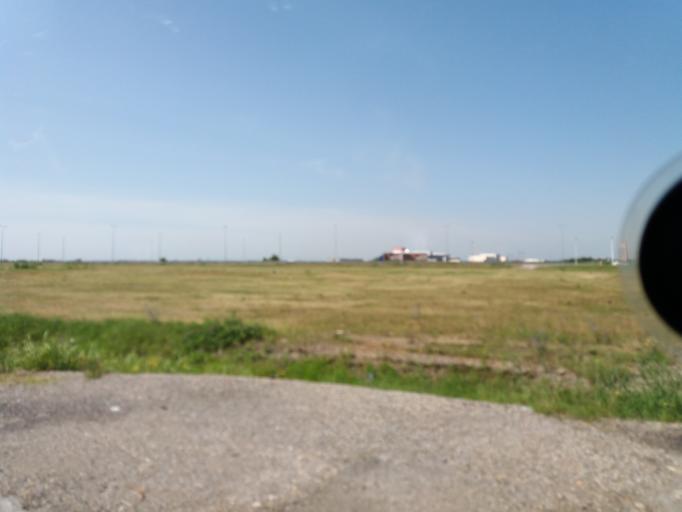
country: RS
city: Simanovci
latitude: 44.8768
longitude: 20.1293
